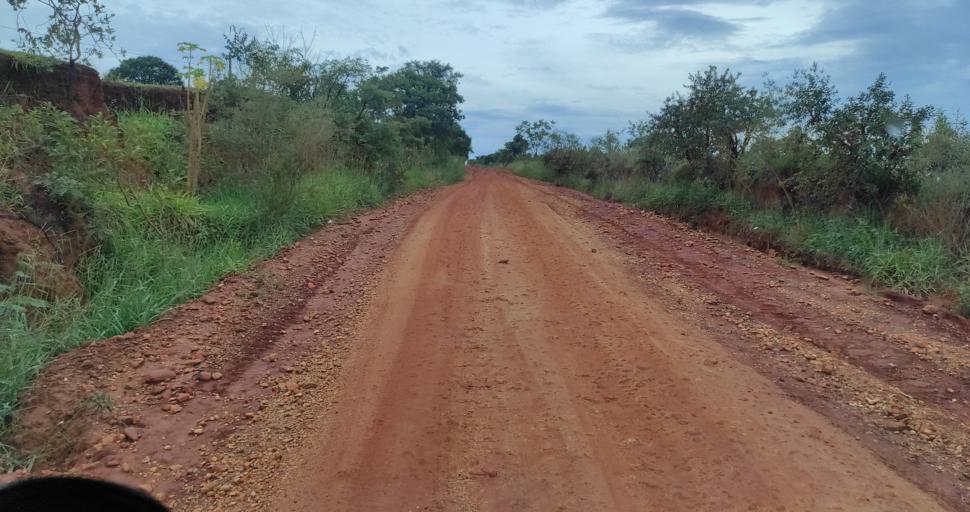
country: BR
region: Minas Gerais
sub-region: Piui
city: Piui
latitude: -20.2966
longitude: -46.3697
